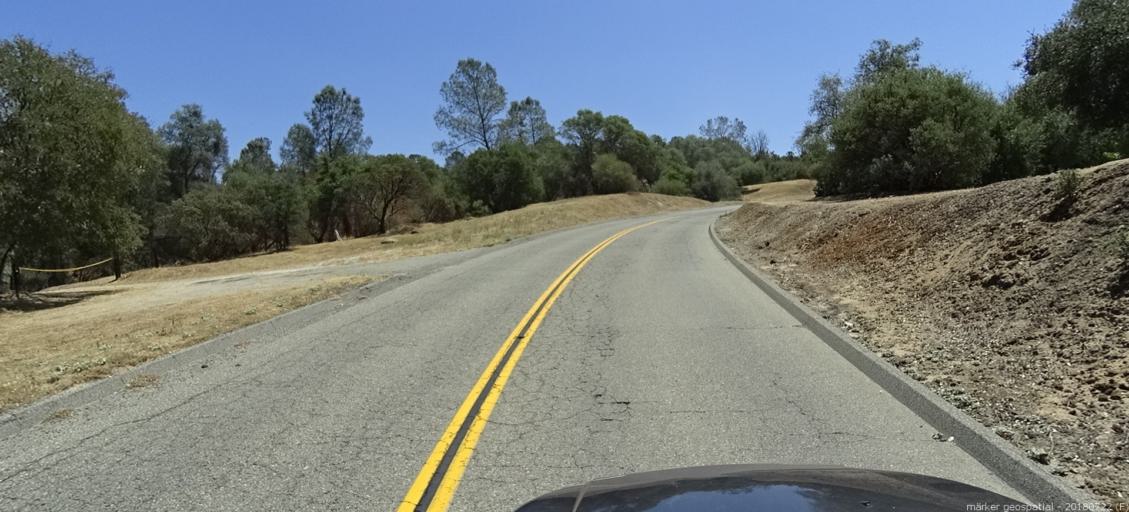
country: US
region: California
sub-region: Madera County
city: Yosemite Lakes
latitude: 37.2054
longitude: -119.7231
